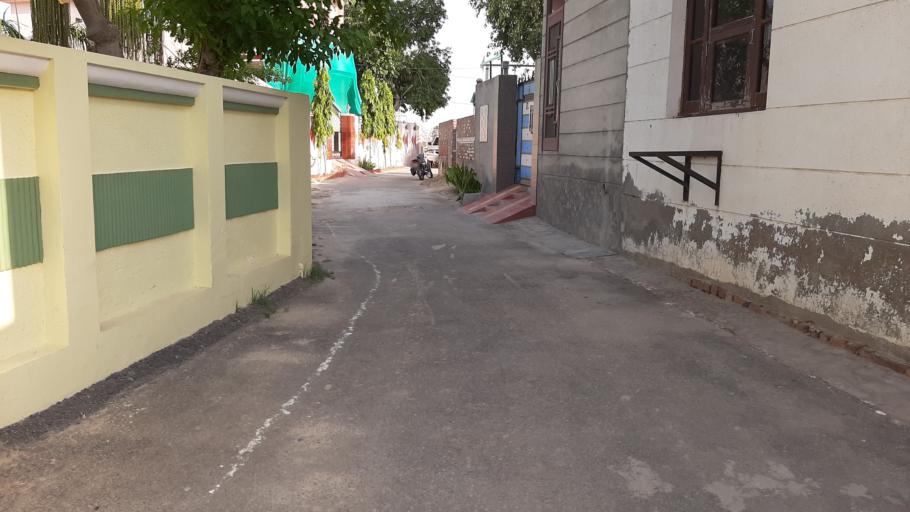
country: IN
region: Punjab
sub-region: Sangrur
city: Sunam
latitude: 30.1397
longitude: 75.8299
